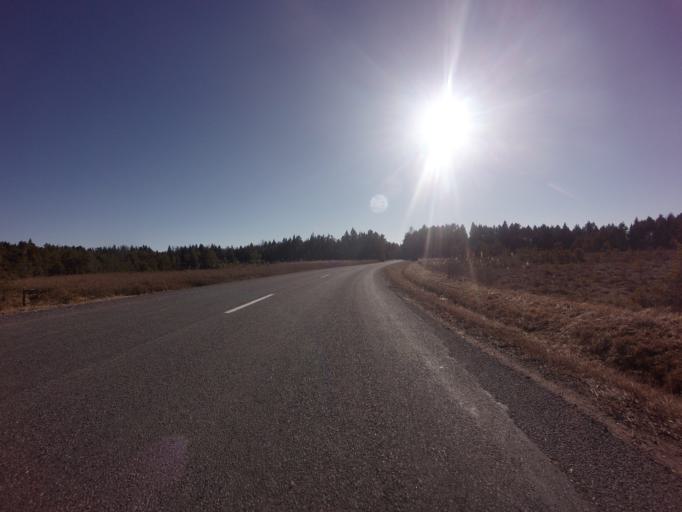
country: EE
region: Saare
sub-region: Kuressaare linn
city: Kuressaare
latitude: 58.5068
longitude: 22.3136
